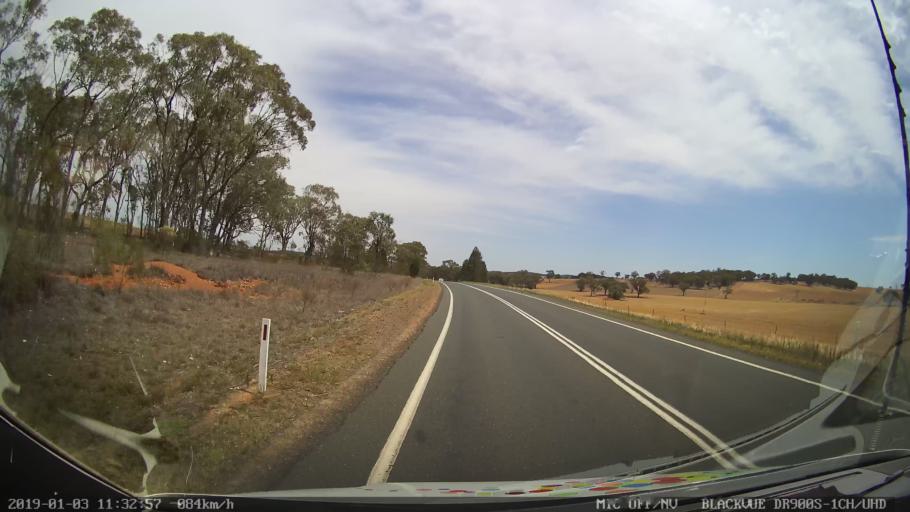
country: AU
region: New South Wales
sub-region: Weddin
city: Grenfell
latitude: -33.9520
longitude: 148.1756
